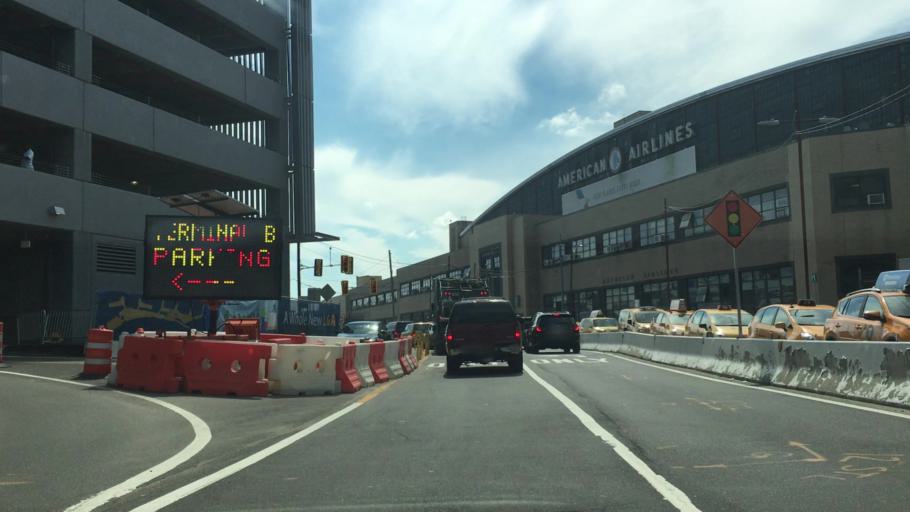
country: US
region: New York
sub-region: Bronx
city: The Bronx
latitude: 40.7734
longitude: -73.8759
